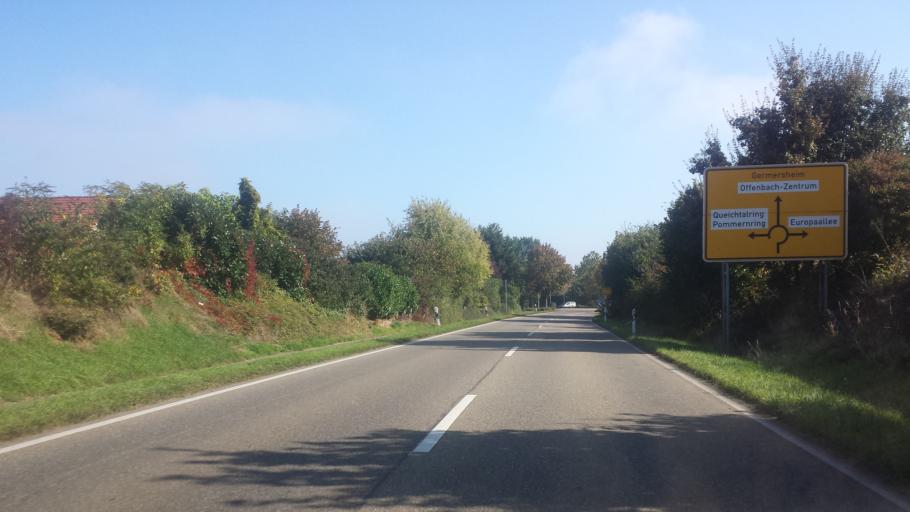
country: DE
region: Rheinland-Pfalz
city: Offenbach an der Queich
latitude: 49.1950
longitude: 8.1845
